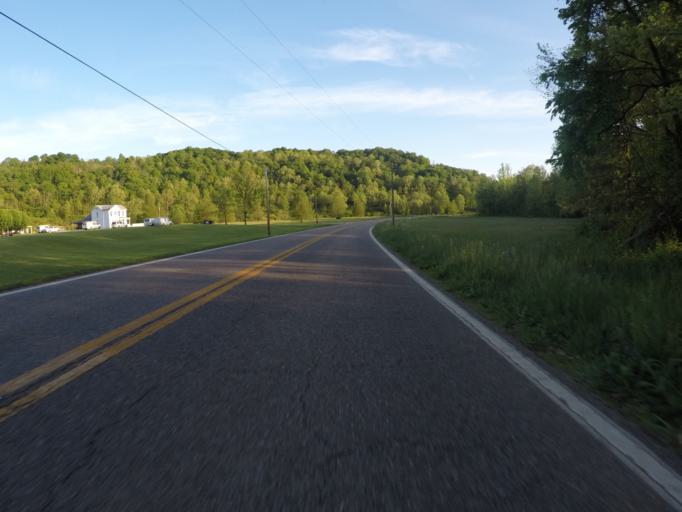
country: US
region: West Virginia
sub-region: Cabell County
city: Huntington
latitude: 38.5128
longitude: -82.4738
